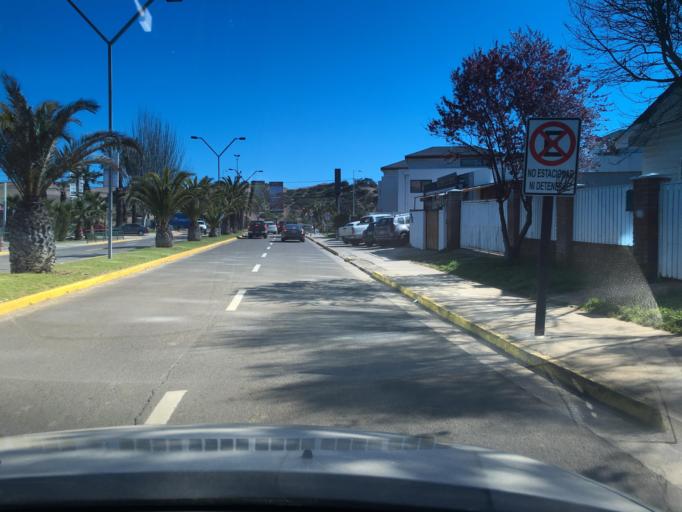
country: CL
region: Valparaiso
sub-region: Provincia de Valparaiso
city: Vina del Mar
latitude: -32.9414
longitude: -71.5456
